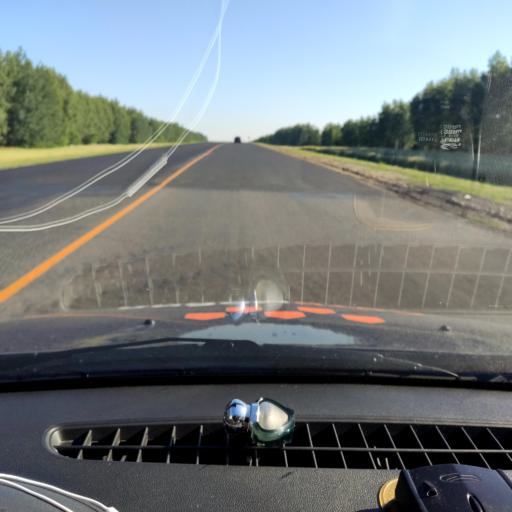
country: RU
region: Orjol
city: Zmiyevka
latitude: 52.7623
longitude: 36.3211
